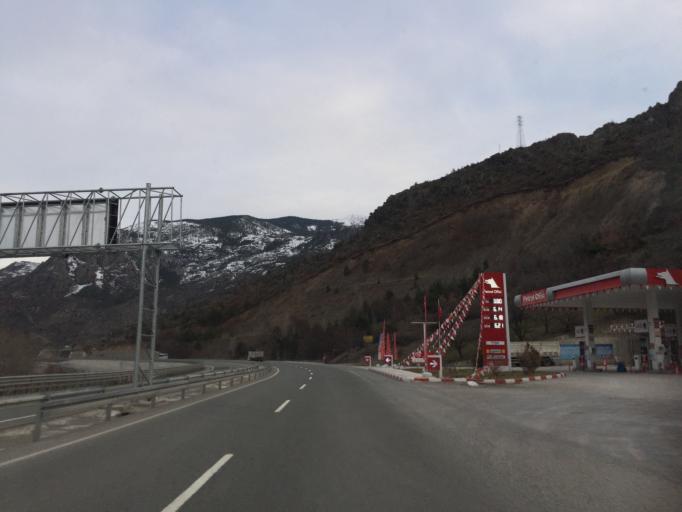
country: TR
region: Gumushane
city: Gumushkhane
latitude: 40.5065
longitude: 39.4228
